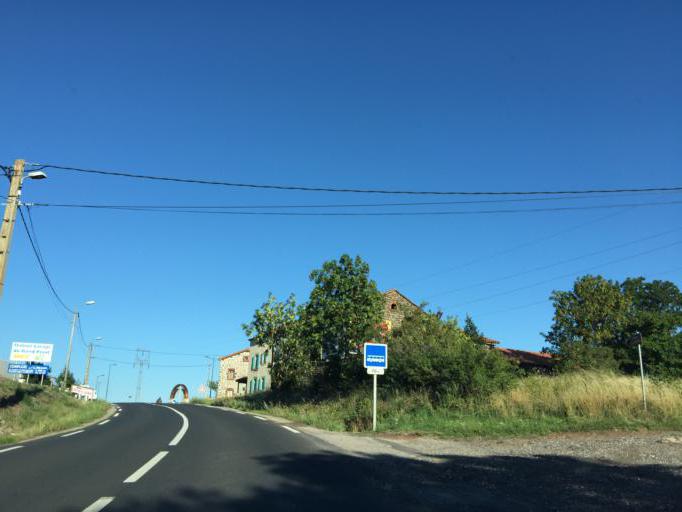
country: FR
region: Auvergne
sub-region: Departement de la Haute-Loire
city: Bains
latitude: 45.0101
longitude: 3.8027
